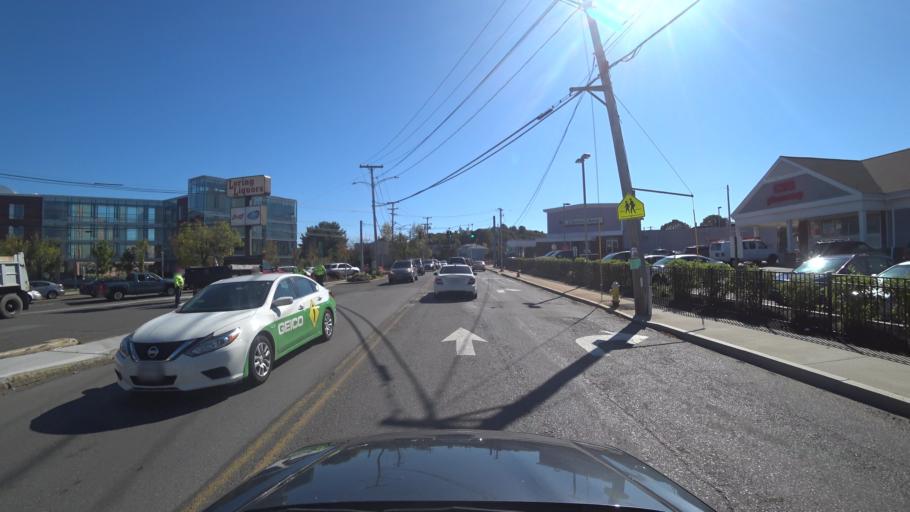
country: US
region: Massachusetts
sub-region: Essex County
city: Salem
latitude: 42.5012
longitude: -70.8960
